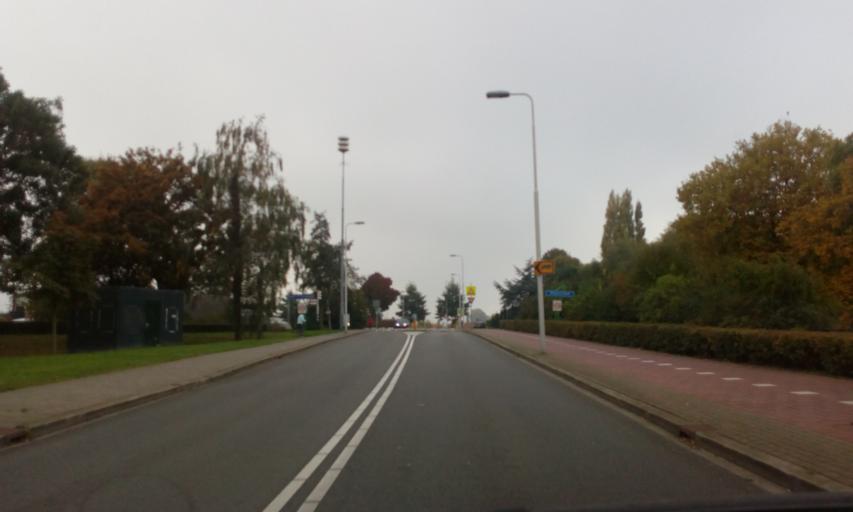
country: NL
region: South Holland
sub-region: Gemeente Lansingerland
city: Berkel en Rodenrijs
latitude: 51.9977
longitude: 4.4869
